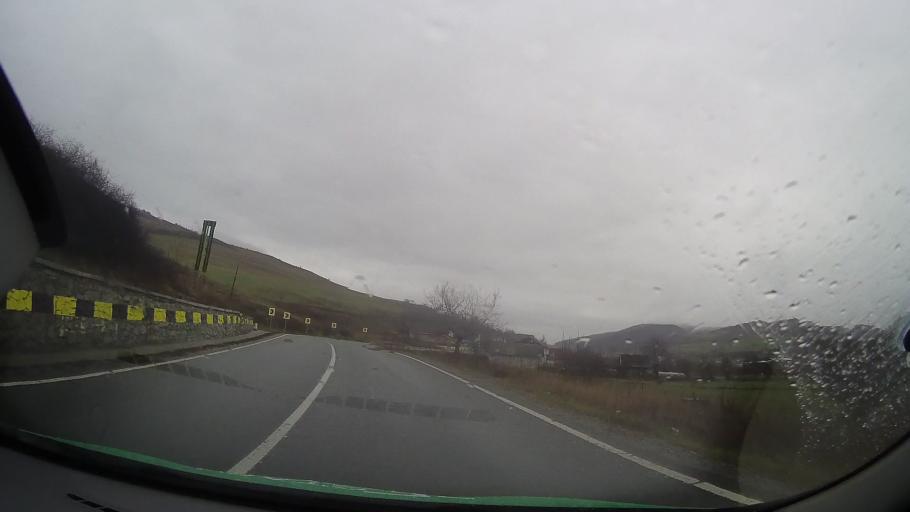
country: RO
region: Bistrita-Nasaud
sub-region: Comuna Galatii Bistritei
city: Galatii Bistritei
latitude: 46.9529
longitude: 24.4474
